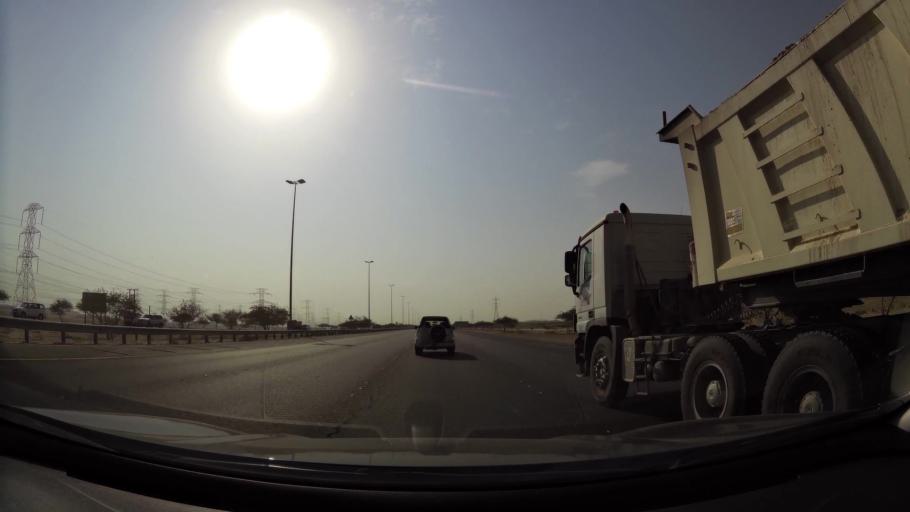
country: KW
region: Al Ahmadi
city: Al Ahmadi
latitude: 28.9786
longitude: 48.1091
